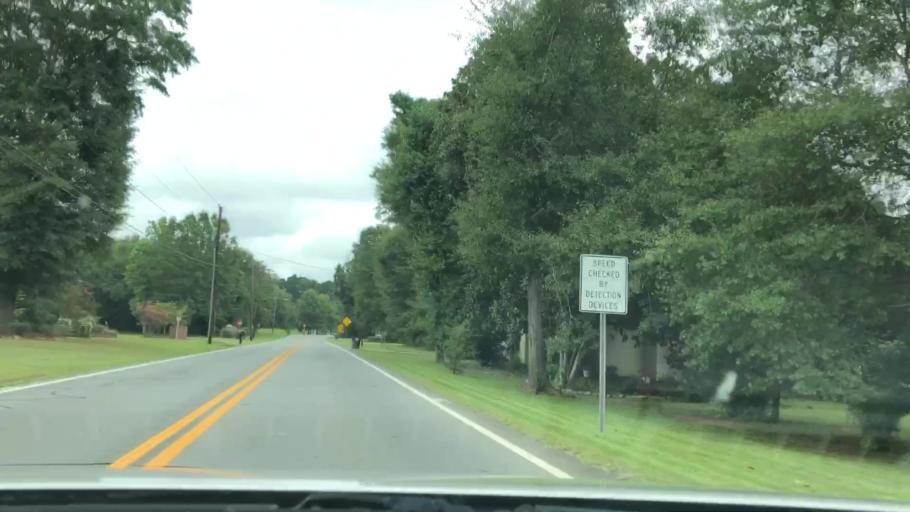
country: US
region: Georgia
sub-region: Pike County
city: Zebulon
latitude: 33.0869
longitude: -84.4466
